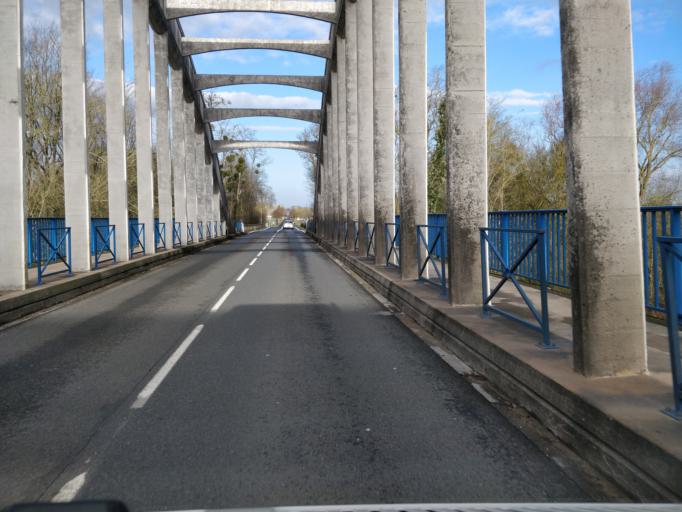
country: FR
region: Centre
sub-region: Departement du Loir-et-Cher
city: Muides-sur-Loire
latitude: 47.6772
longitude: 1.5249
